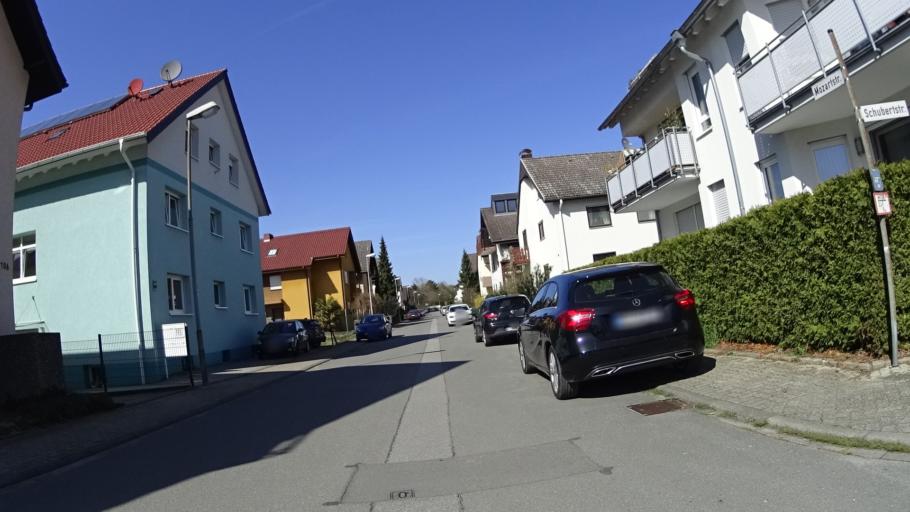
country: DE
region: Baden-Wuerttemberg
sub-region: Karlsruhe Region
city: Schriesheim
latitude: 49.4770
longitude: 8.6510
